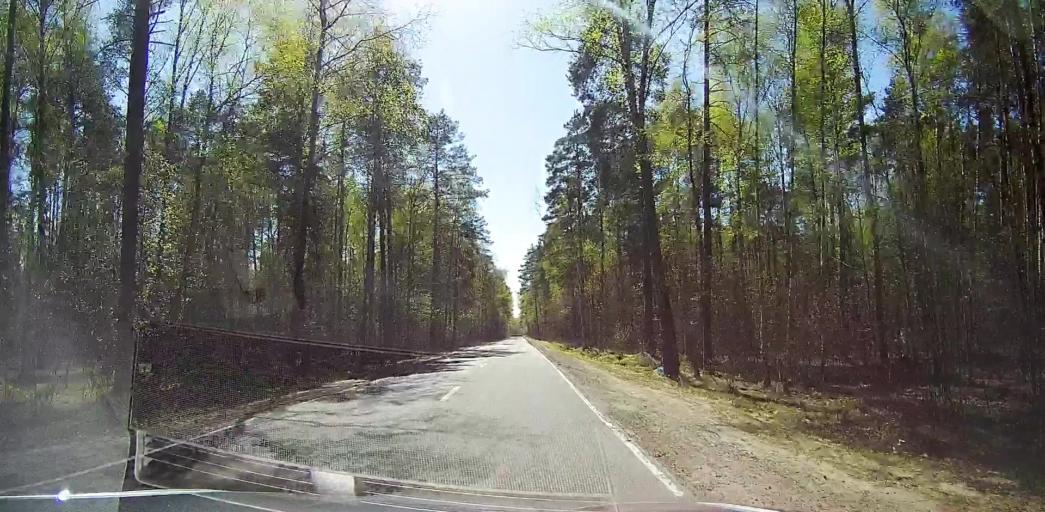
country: RU
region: Moskovskaya
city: Beloozerskiy
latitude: 55.4832
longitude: 38.4249
